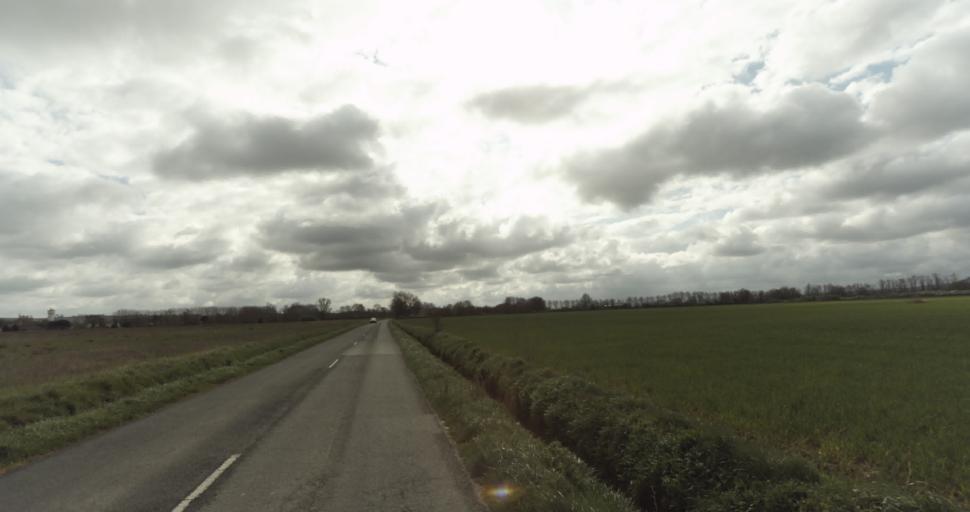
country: FR
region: Midi-Pyrenees
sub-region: Departement de la Haute-Garonne
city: Auterive
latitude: 43.3598
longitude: 1.4481
